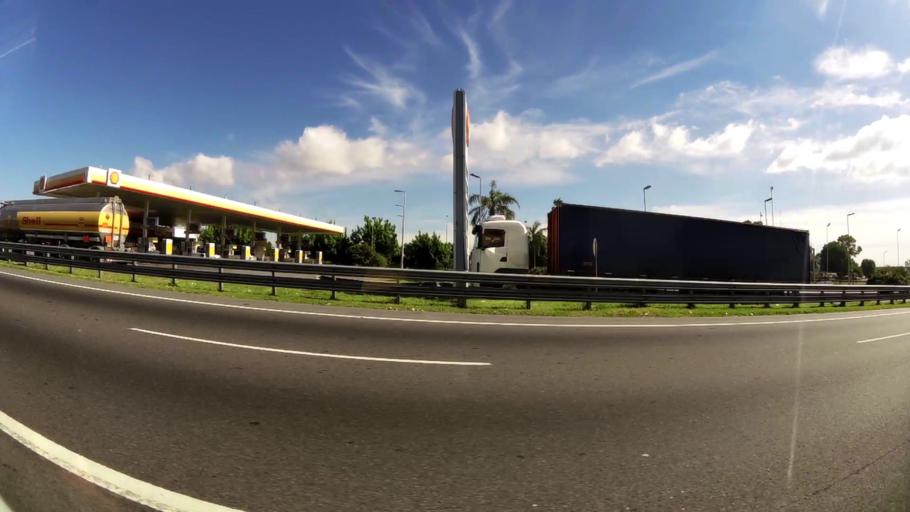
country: AR
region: Buenos Aires
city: Caseros
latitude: -34.6296
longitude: -58.5572
